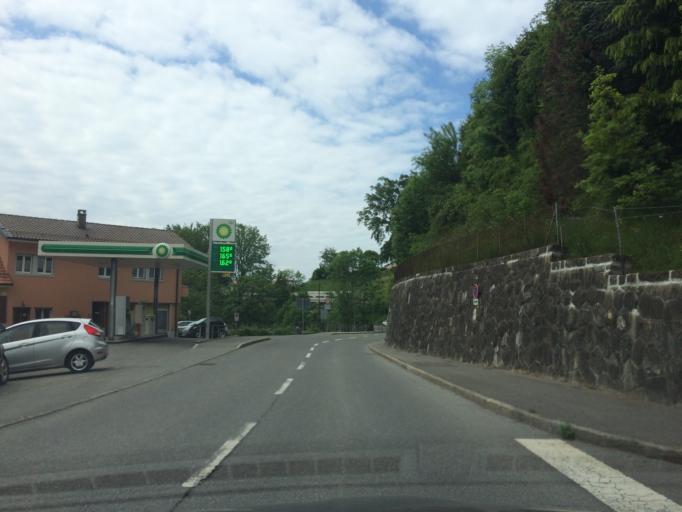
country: CH
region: Vaud
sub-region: Lavaux-Oron District
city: Chexbres
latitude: 46.4819
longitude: 6.7749
